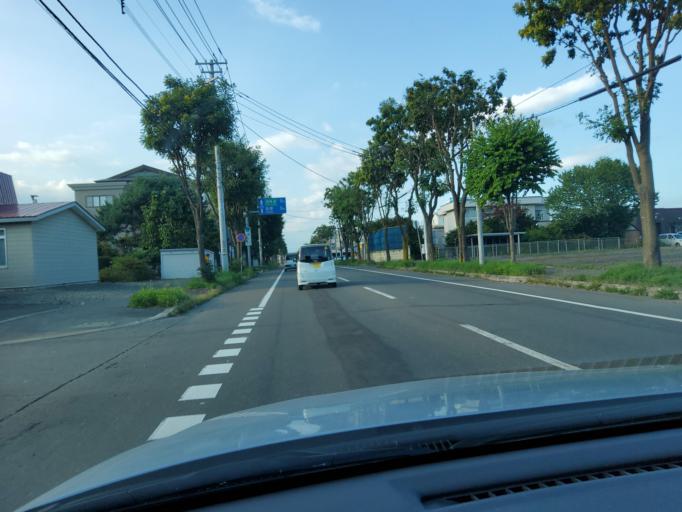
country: JP
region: Hokkaido
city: Obihiro
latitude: 42.9318
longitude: 143.1849
